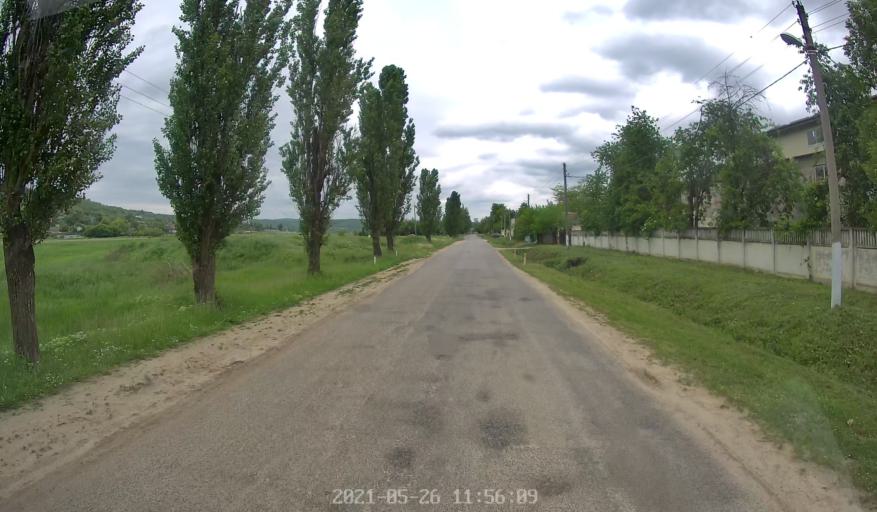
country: MD
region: Hincesti
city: Dancu
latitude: 46.7820
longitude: 28.3490
